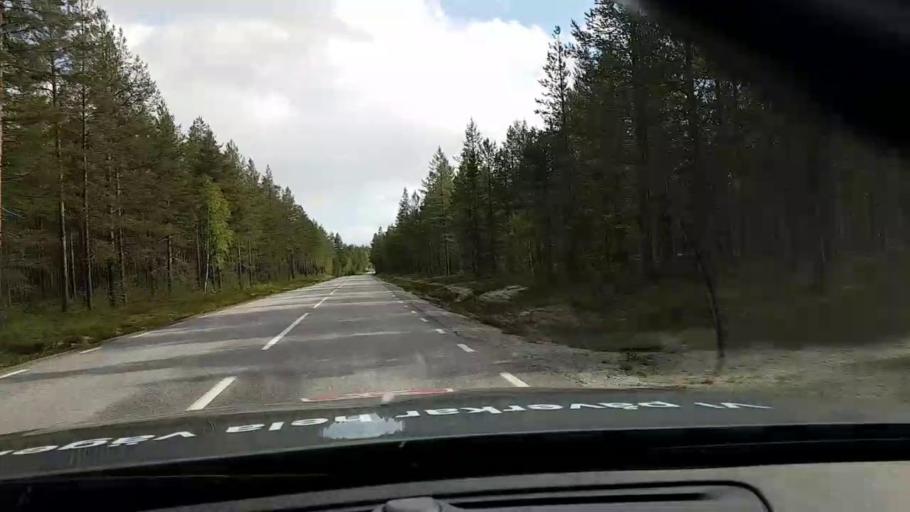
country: SE
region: Vaesternorrland
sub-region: OErnskoeldsviks Kommun
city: Bredbyn
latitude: 63.6527
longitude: 17.8869
